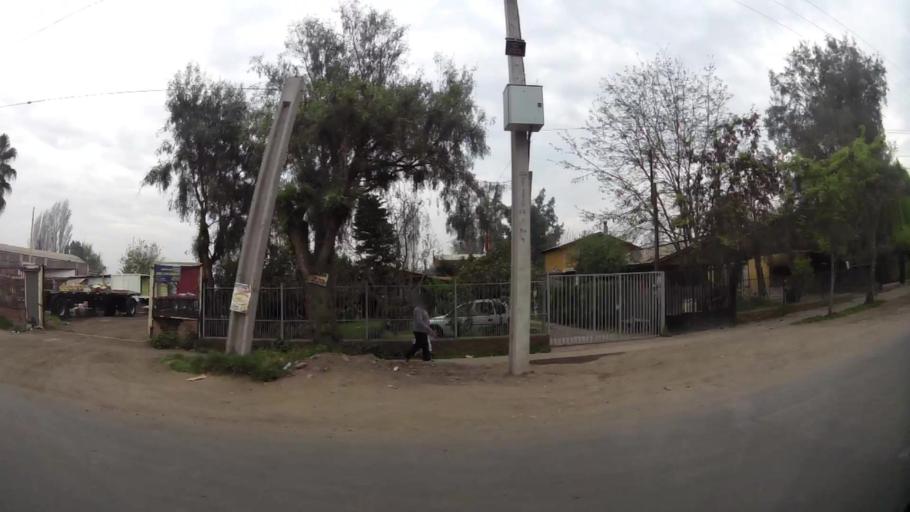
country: CL
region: Santiago Metropolitan
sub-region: Provincia de Chacabuco
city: Chicureo Abajo
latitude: -33.2724
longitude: -70.7454
